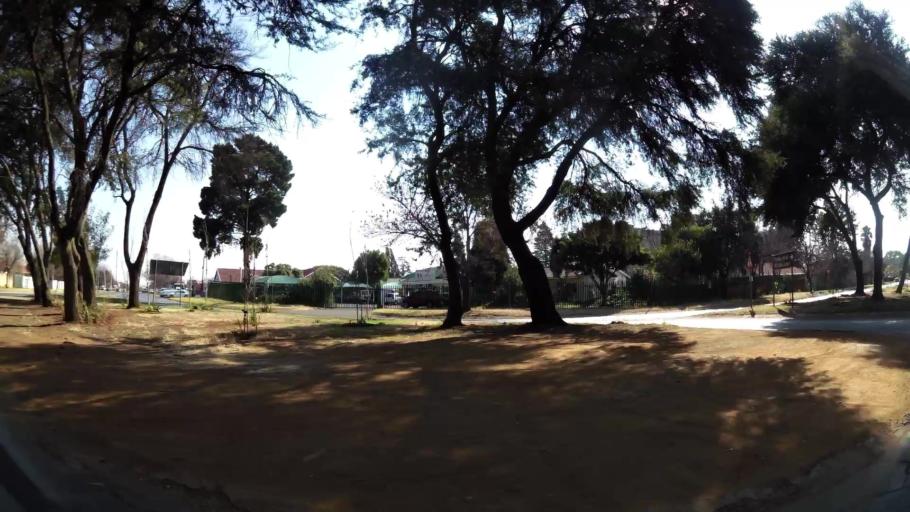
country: ZA
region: Gauteng
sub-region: City of Johannesburg Metropolitan Municipality
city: Modderfontein
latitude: -26.1238
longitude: 28.2322
